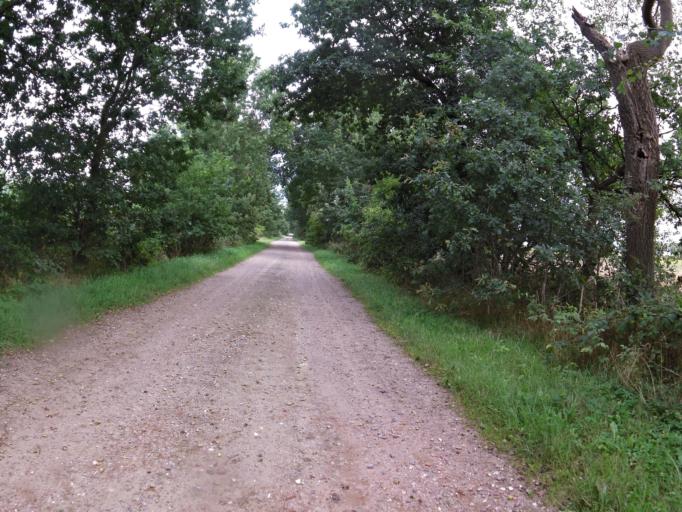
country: DE
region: Lower Saxony
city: Oerel
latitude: 53.4930
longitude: 9.0567
